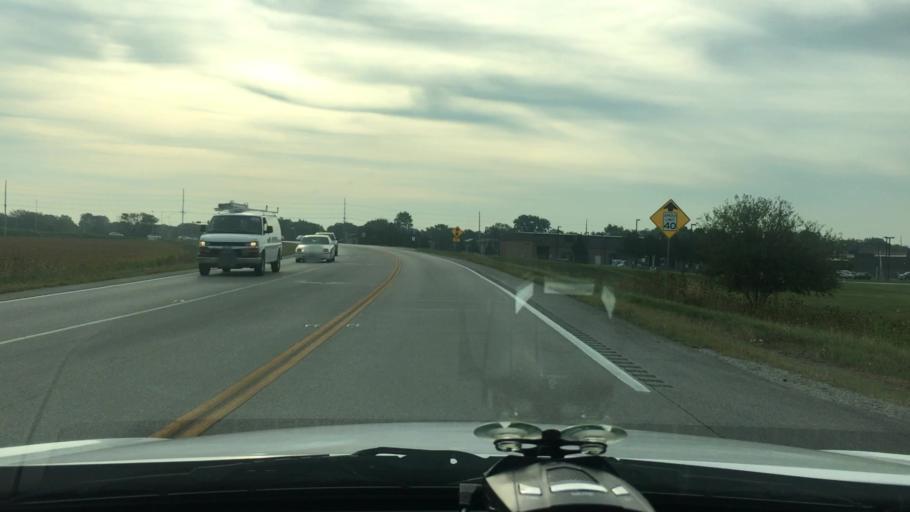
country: US
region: Illinois
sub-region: Champaign County
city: Champaign
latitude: 40.1395
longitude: -88.2813
